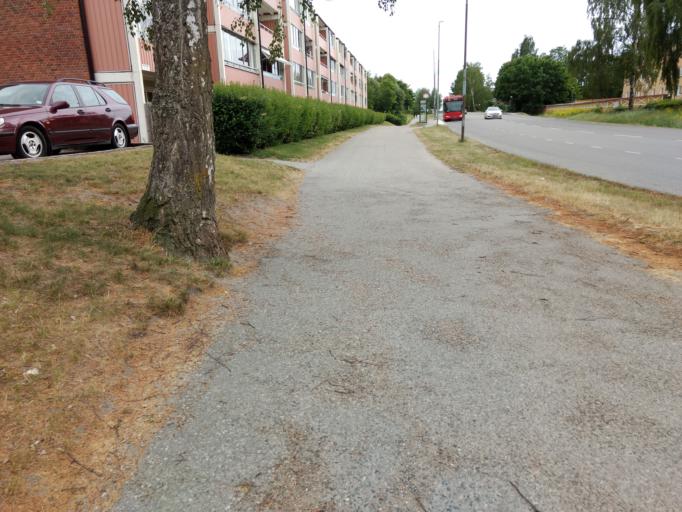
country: SE
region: Stockholm
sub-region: Upplands Vasby Kommun
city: Upplands Vaesby
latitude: 59.5231
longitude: 17.9168
